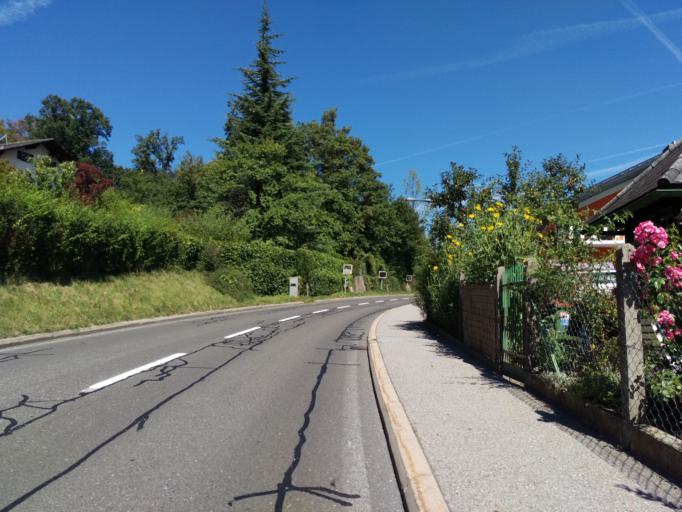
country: AT
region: Styria
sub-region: Politischer Bezirk Graz-Umgebung
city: Nestelbach bei Graz
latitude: 47.0669
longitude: 15.5883
